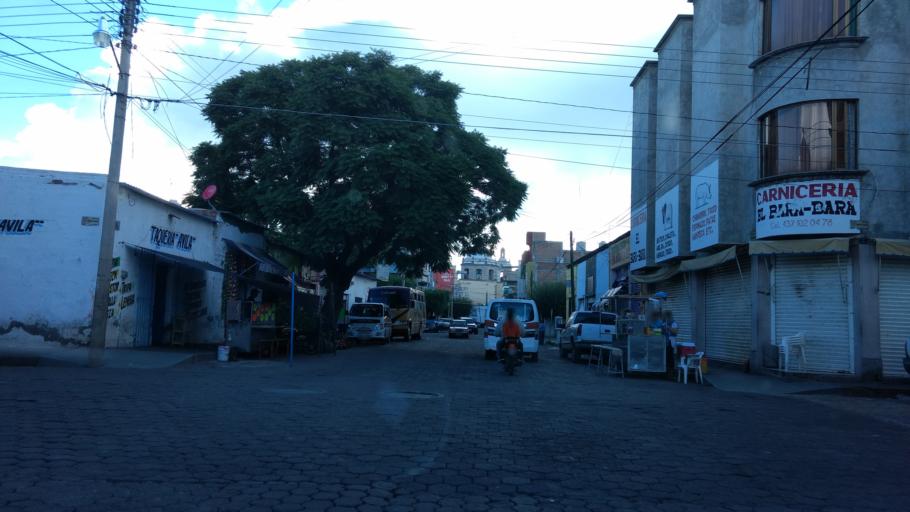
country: MX
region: Zacatecas
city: Tlaltenango de Sanchez Roman
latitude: 21.7817
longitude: -103.3037
